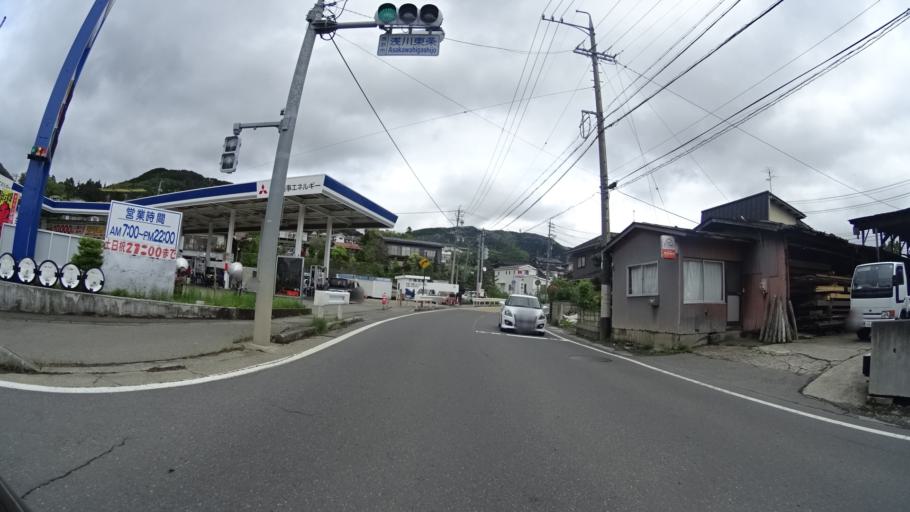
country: JP
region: Nagano
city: Nagano-shi
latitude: 36.6816
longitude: 138.2010
